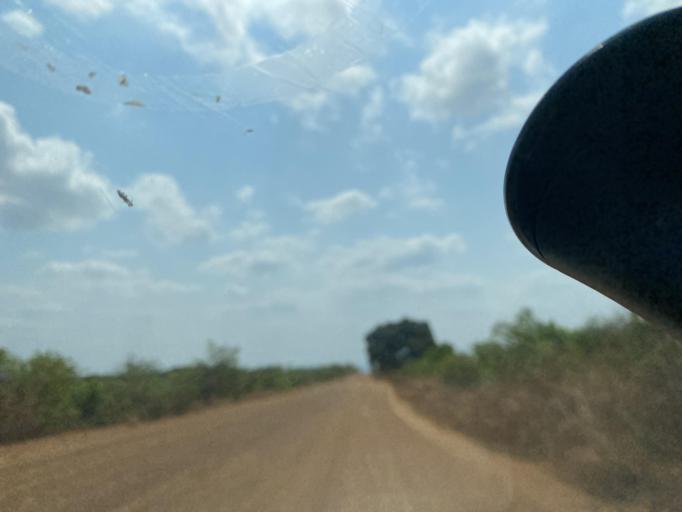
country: ZM
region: Lusaka
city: Chongwe
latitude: -15.5927
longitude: 28.7919
